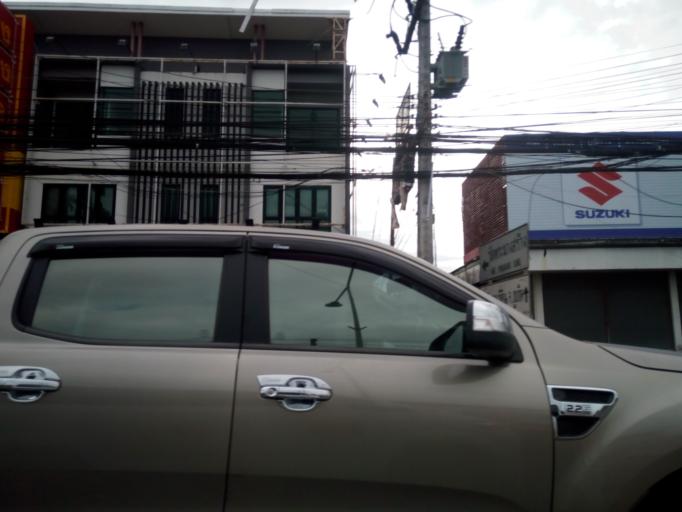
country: TH
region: Phuket
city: Thalang
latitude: 8.0242
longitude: 98.3338
